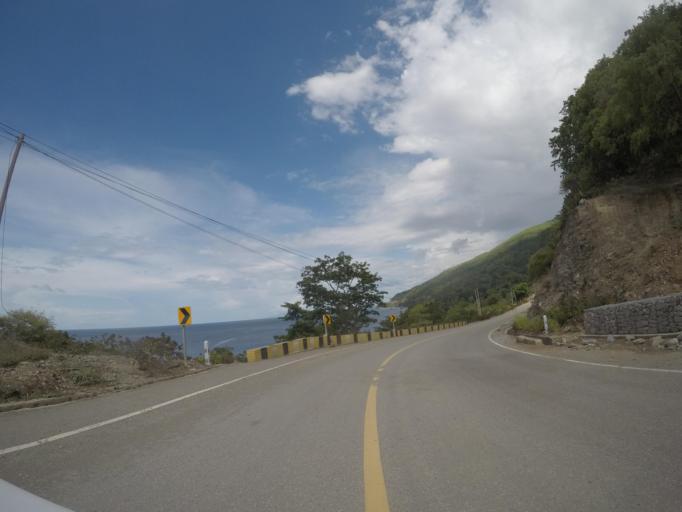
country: TL
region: Liquica
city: Maubara
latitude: -8.6381
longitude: 125.1319
